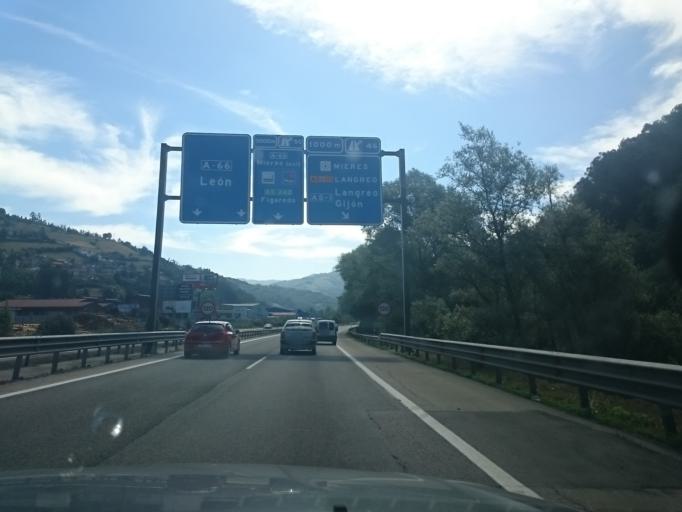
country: ES
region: Asturias
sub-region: Province of Asturias
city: Mieres
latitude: 43.2686
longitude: -5.8012
